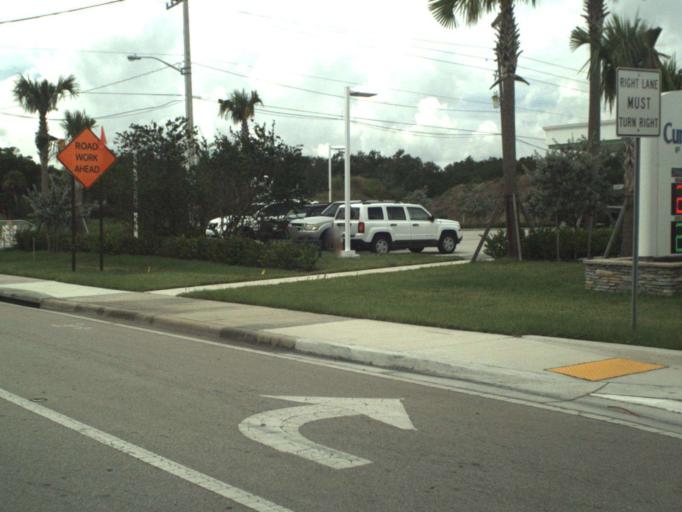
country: US
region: Florida
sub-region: Saint Lucie County
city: White City
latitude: 27.3748
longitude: -80.3505
